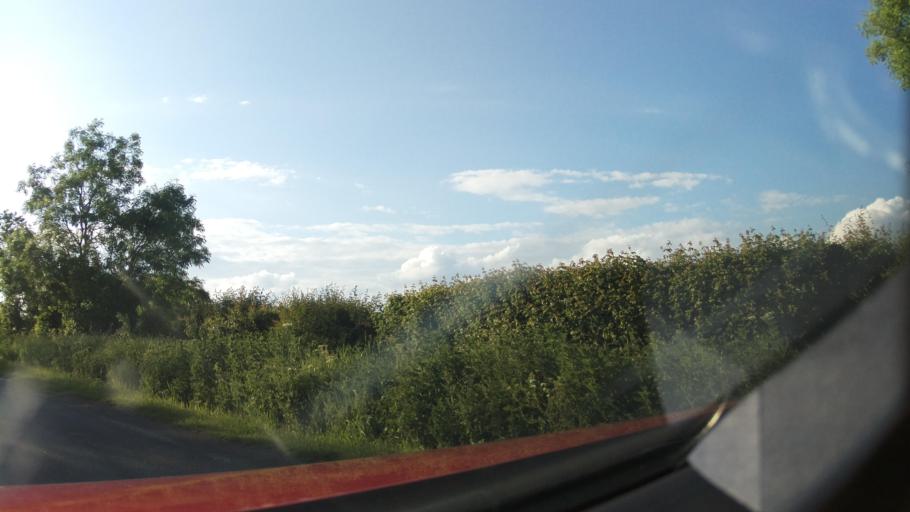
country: GB
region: England
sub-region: Lincolnshire
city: Navenby
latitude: 53.1172
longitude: -0.6233
